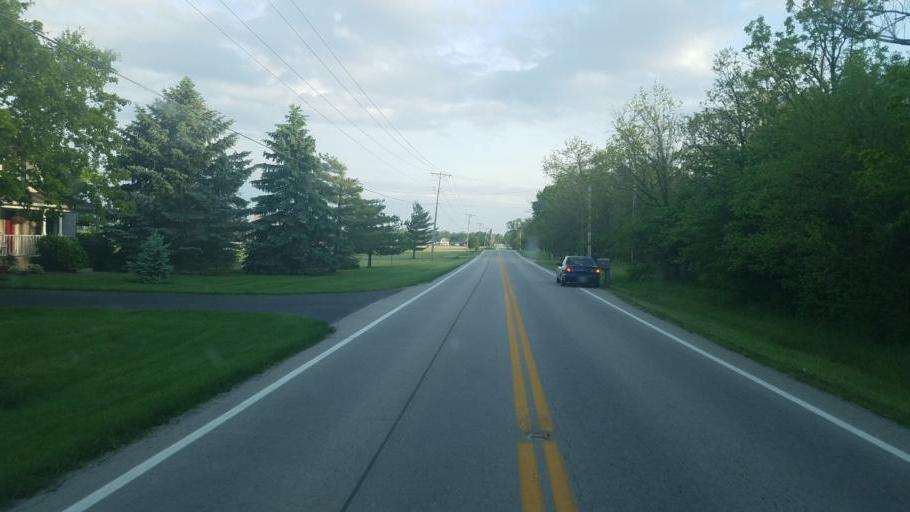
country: US
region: Ohio
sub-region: Clinton County
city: Sabina
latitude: 39.4674
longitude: -83.6655
